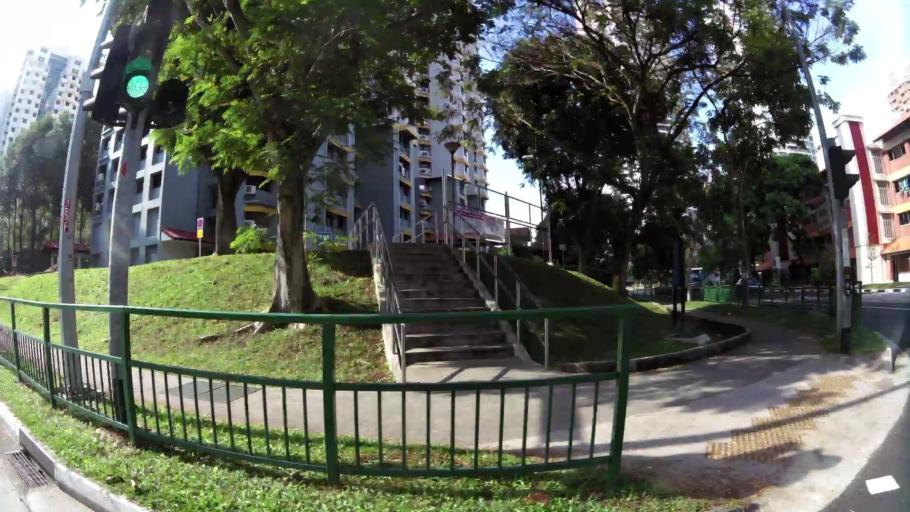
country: SG
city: Singapore
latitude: 1.3574
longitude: 103.8451
